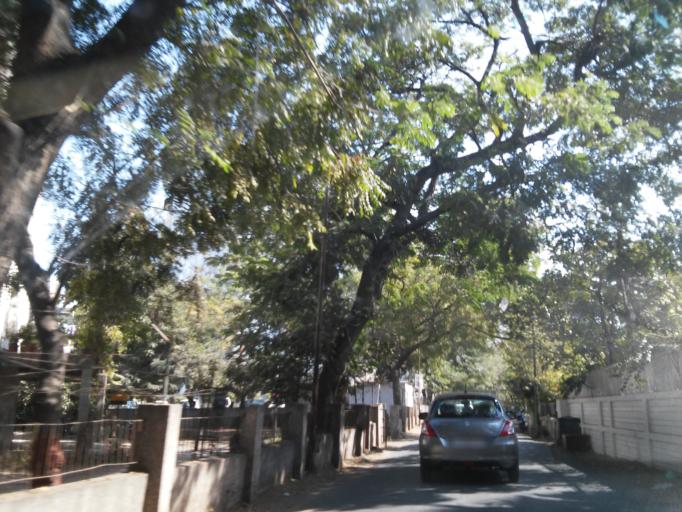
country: IN
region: Gujarat
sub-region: Ahmadabad
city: Sarkhej
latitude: 23.0261
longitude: 72.5310
